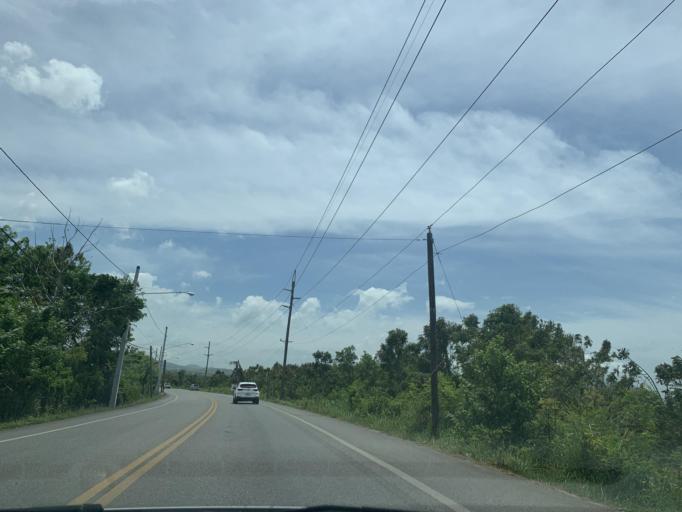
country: DO
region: Puerto Plata
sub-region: Puerto Plata
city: Puerto Plata
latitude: 19.7478
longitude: -70.5968
